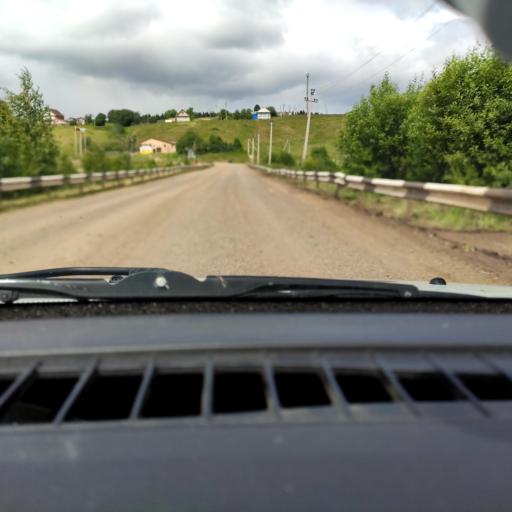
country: RU
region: Perm
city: Uinskoye
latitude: 57.1184
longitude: 56.5224
